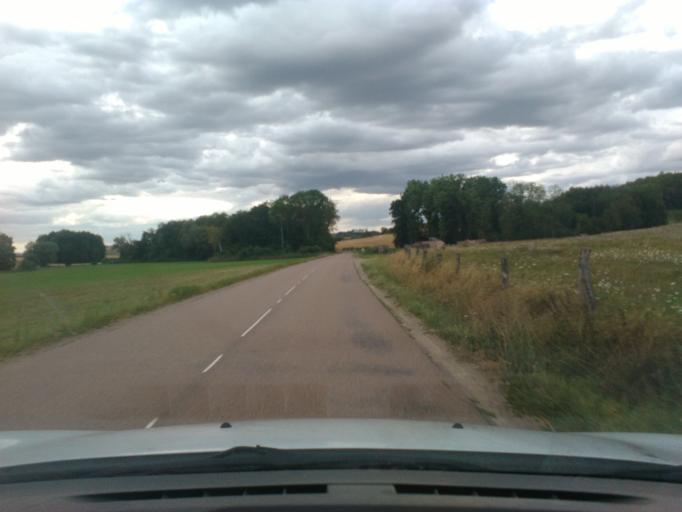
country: FR
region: Lorraine
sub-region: Departement des Vosges
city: Charmes
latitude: 48.3486
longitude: 6.2766
